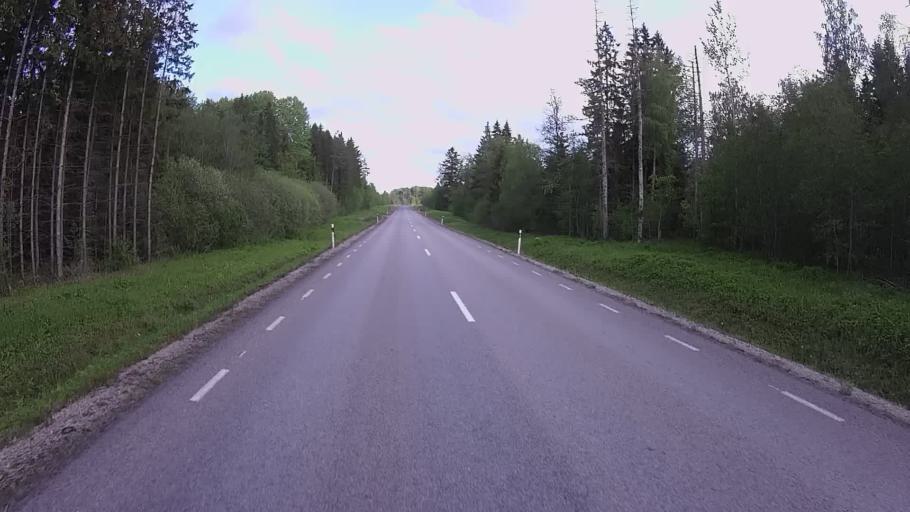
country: EE
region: Jogevamaa
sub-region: Mustvee linn
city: Mustvee
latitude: 59.0595
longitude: 27.0068
